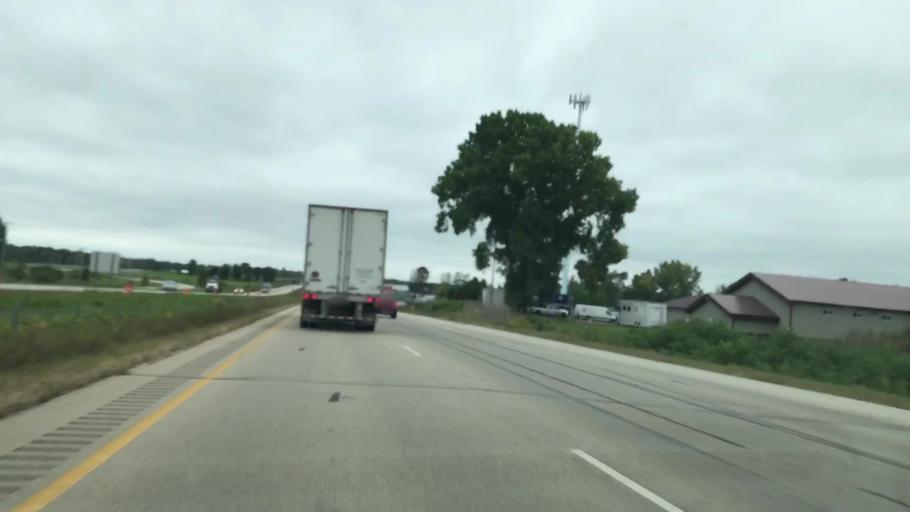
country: US
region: Wisconsin
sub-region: Brown County
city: Suamico
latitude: 44.6717
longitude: -88.0504
